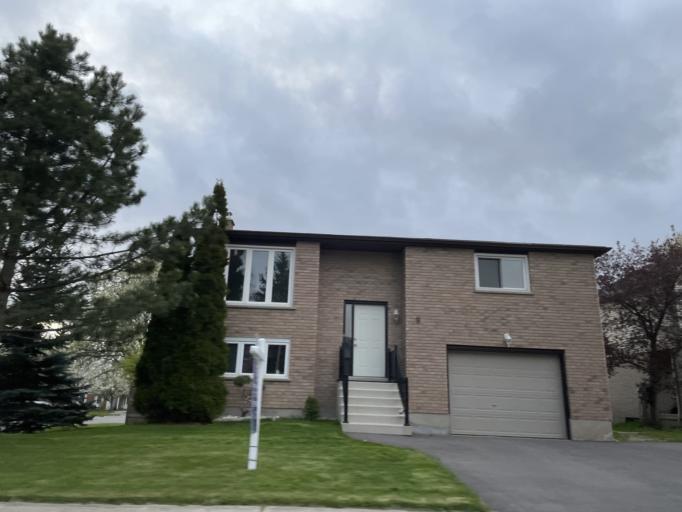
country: CA
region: Ontario
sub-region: Wellington County
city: Guelph
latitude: 43.5247
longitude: -80.2832
